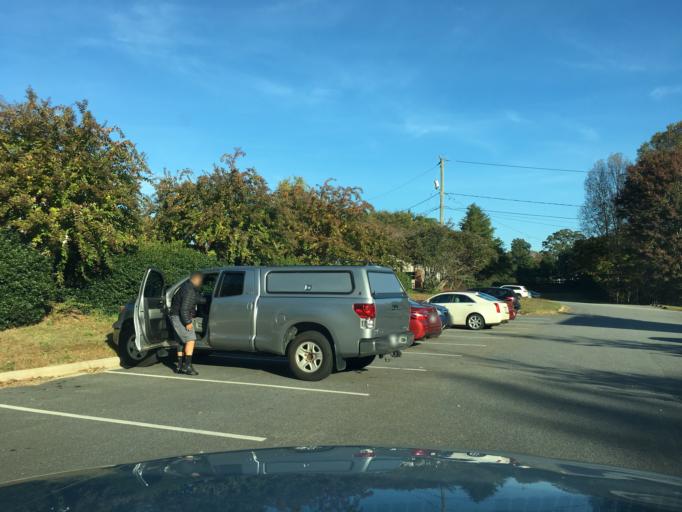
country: US
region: North Carolina
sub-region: Catawba County
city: Conover
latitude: 35.7154
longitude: -81.2647
